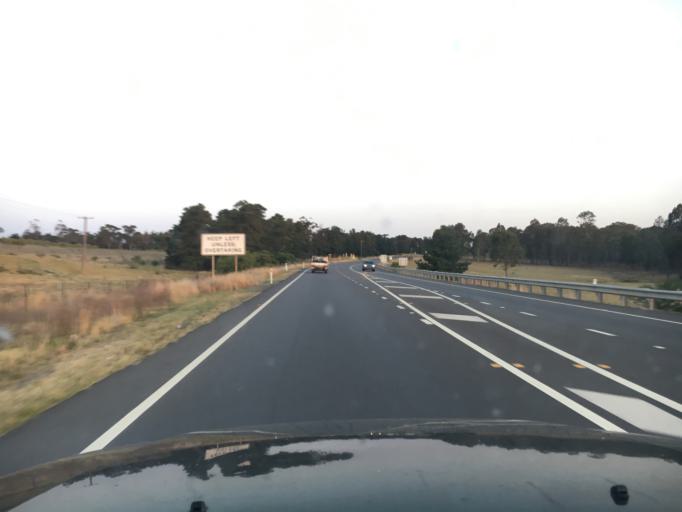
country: AU
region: New South Wales
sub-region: Cessnock
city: Greta
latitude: -32.6868
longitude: 151.3996
